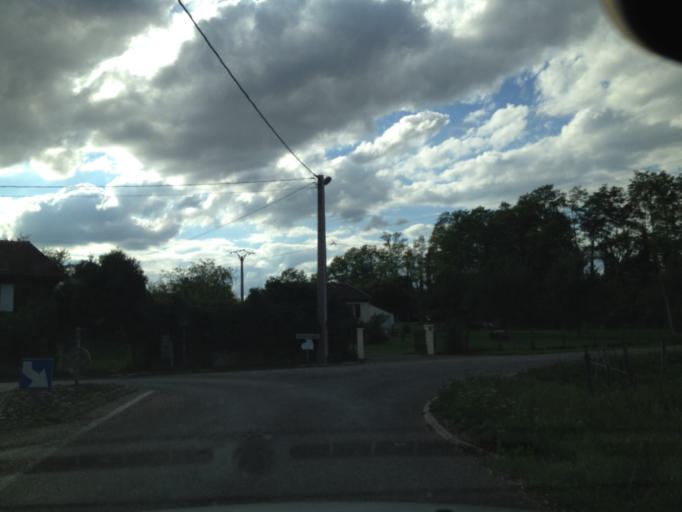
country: FR
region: Franche-Comte
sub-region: Departement de la Haute-Saone
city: Faverney
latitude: 47.7857
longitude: 6.0020
